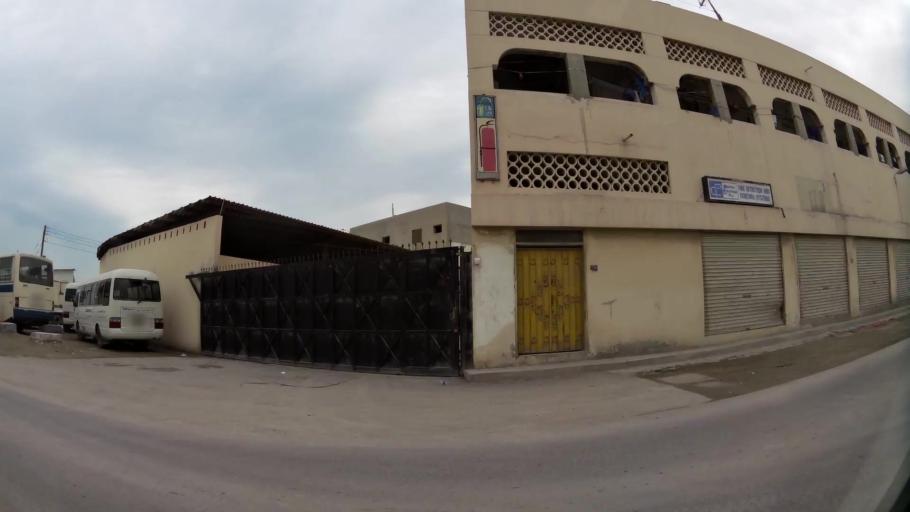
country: BH
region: Northern
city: Sitrah
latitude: 26.1681
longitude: 50.6151
